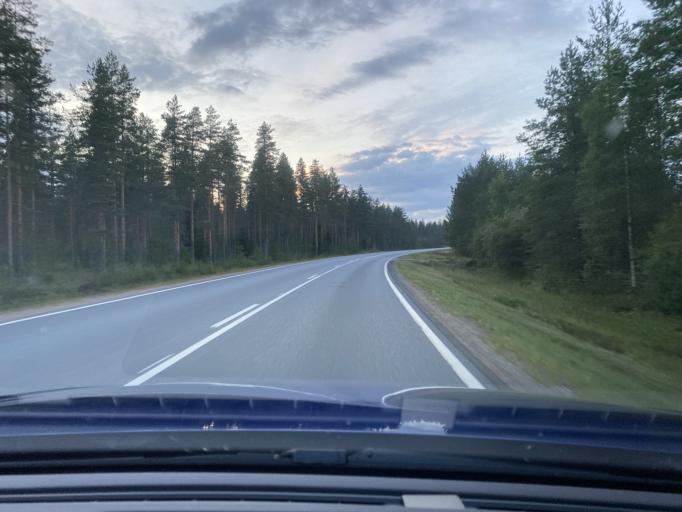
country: FI
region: Satakunta
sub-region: Pohjois-Satakunta
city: Honkajoki
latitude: 62.1248
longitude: 22.2458
